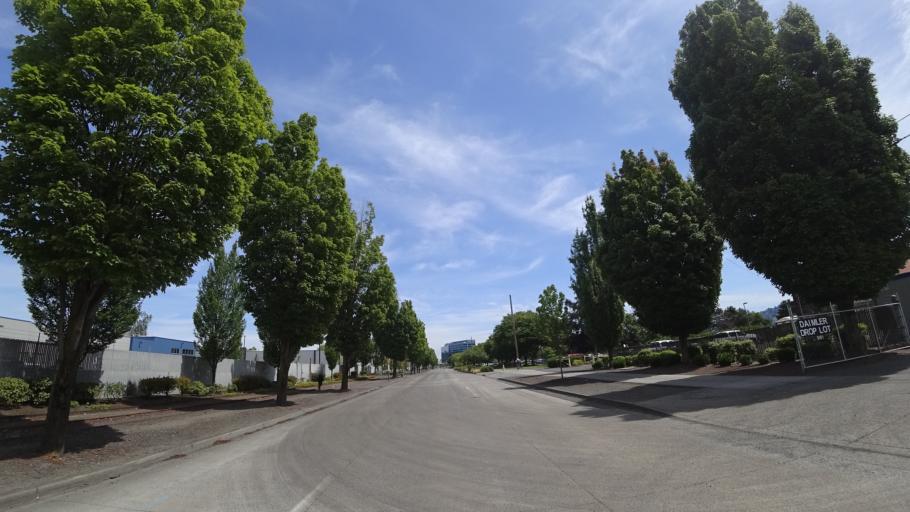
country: US
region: Oregon
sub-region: Multnomah County
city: Portland
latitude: 45.5593
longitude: -122.7098
